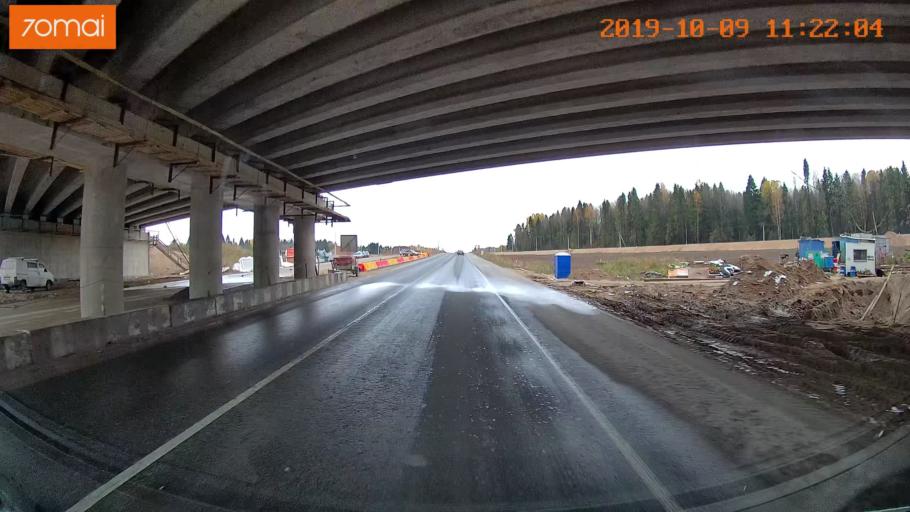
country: RU
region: Vologda
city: Vologda
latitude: 59.1346
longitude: 39.9547
